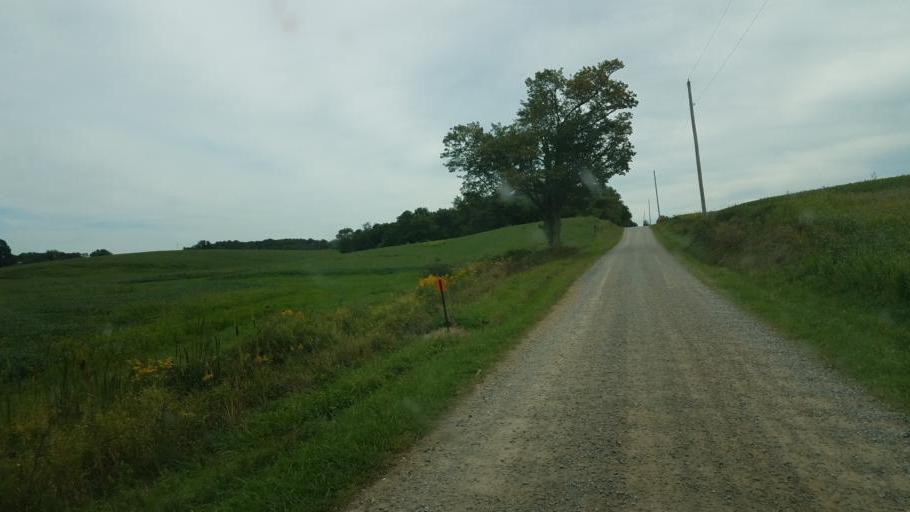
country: US
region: Ohio
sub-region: Knox County
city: Centerburg
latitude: 40.3392
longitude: -82.7141
